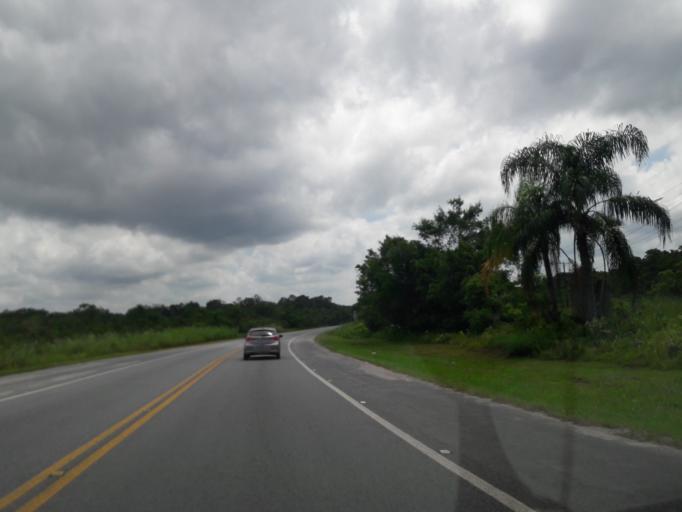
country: BR
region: Parana
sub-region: Pontal Do Parana
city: Pontal do Parana
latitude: -25.6707
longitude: -48.5148
